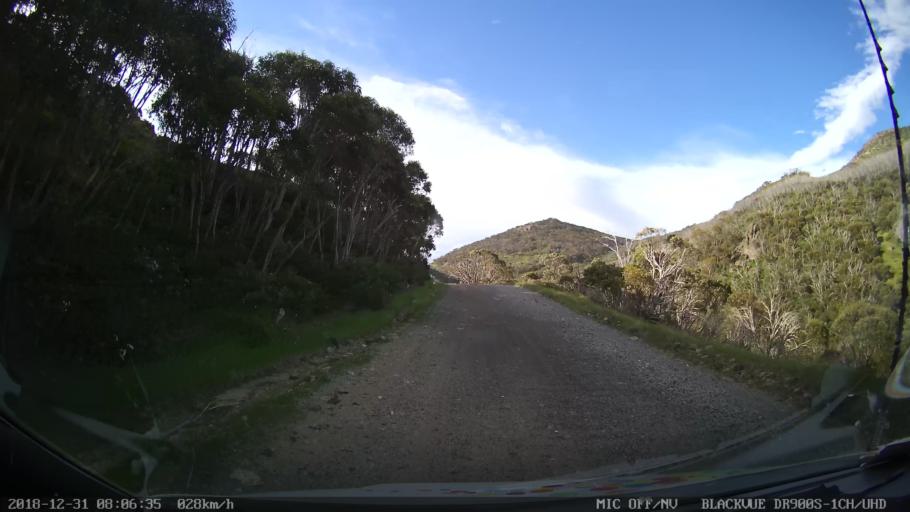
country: AU
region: New South Wales
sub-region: Snowy River
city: Jindabyne
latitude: -36.3753
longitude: 148.4083
